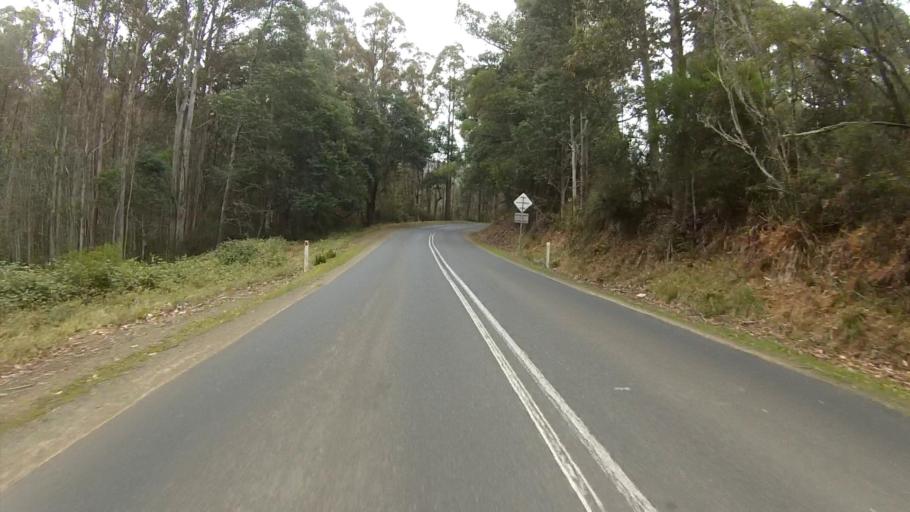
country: AU
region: Tasmania
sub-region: Huon Valley
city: Cygnet
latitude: -43.1458
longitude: 147.1535
